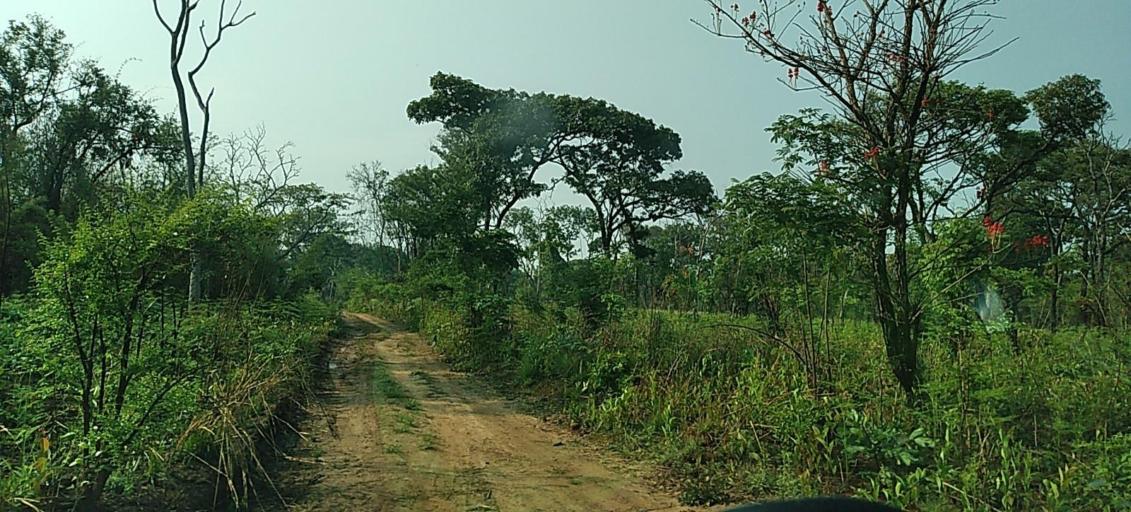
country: ZM
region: North-Western
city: Solwezi
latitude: -12.4019
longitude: 26.5858
